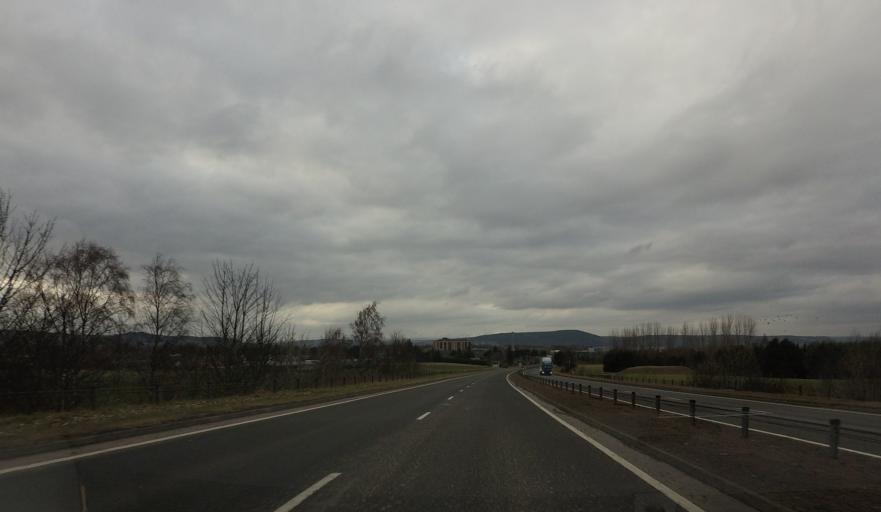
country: GB
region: Scotland
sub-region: Highland
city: Inverness
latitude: 57.4676
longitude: -4.1794
